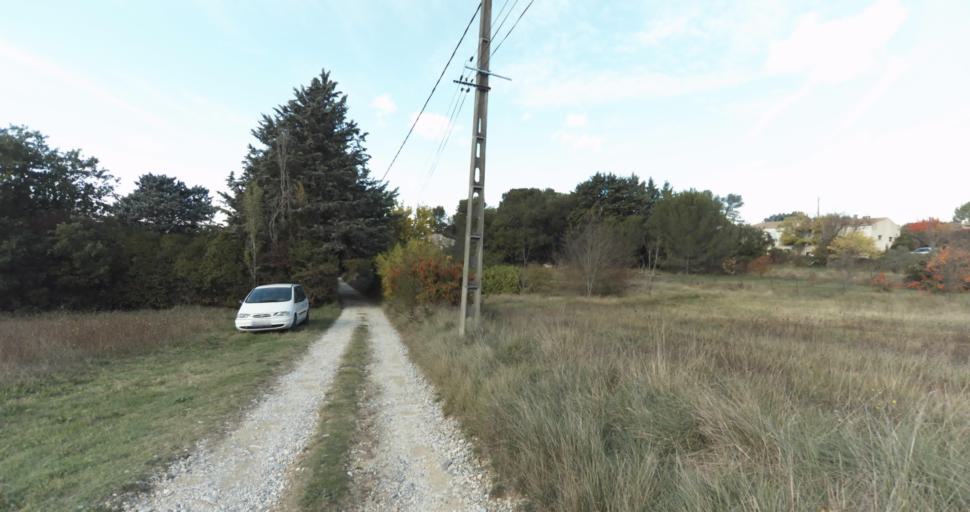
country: FR
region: Provence-Alpes-Cote d'Azur
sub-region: Departement des Bouches-du-Rhone
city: Venelles
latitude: 43.6068
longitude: 5.4911
